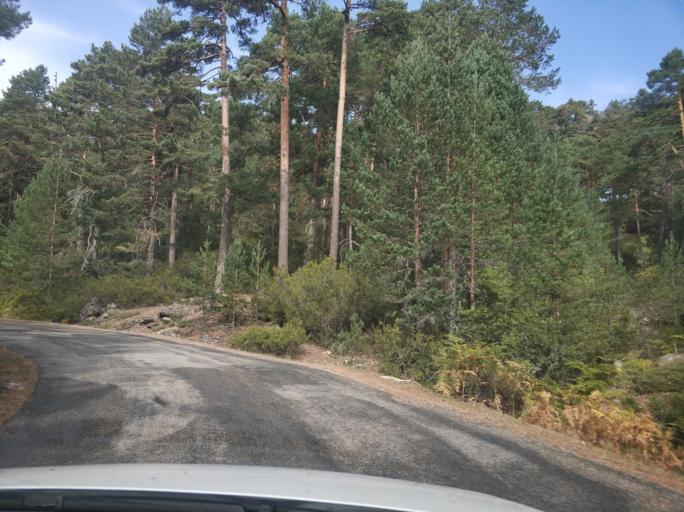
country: ES
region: Castille and Leon
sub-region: Provincia de Soria
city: Duruelo de la Sierra
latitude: 41.9958
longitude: -2.9148
